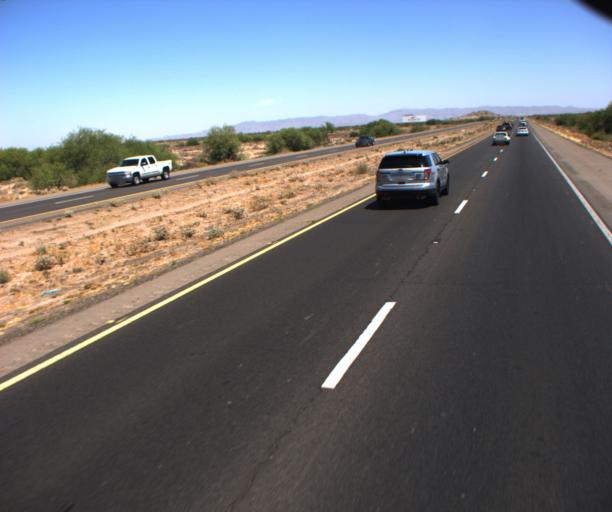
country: US
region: Arizona
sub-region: Pinal County
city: Maricopa
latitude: 33.1483
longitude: -112.0069
